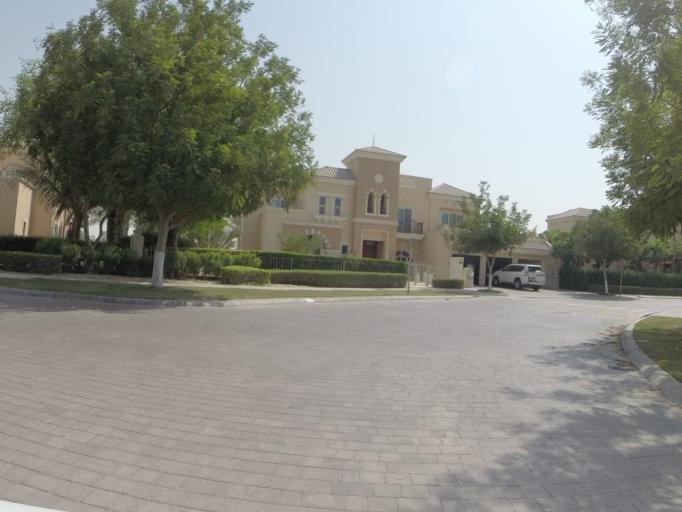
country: AE
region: Dubai
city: Dubai
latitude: 25.0325
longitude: 55.2155
